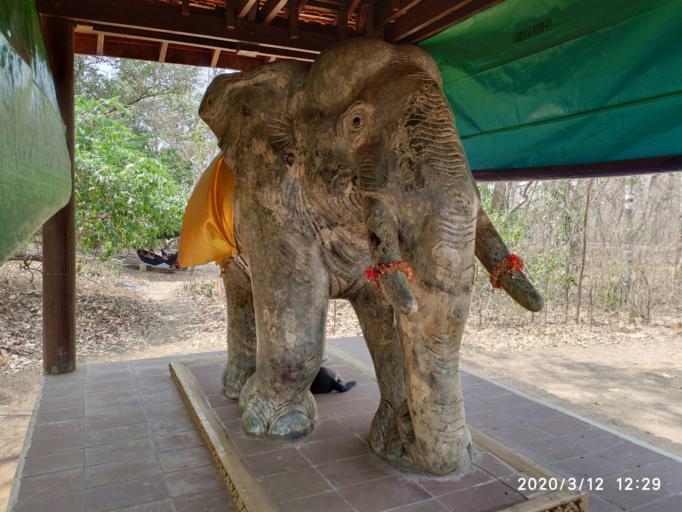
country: KH
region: Preah Vihear
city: Tbeng Meanchey
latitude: 13.7835
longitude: 104.5366
